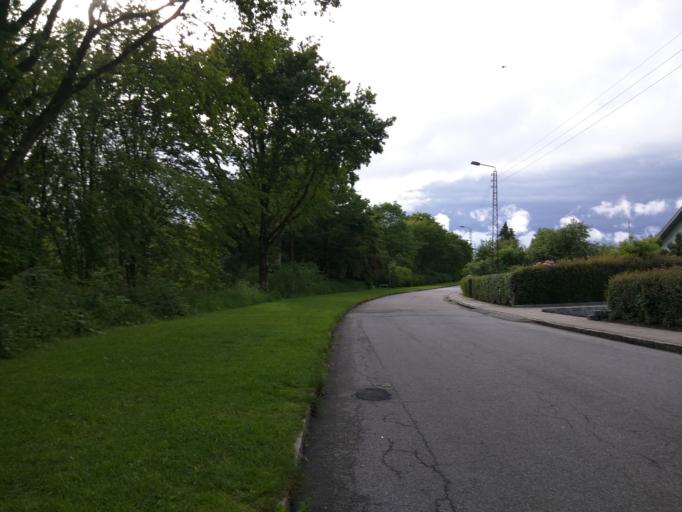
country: DK
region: Central Jutland
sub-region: Viborg Kommune
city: Viborg
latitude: 56.4516
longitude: 9.3864
